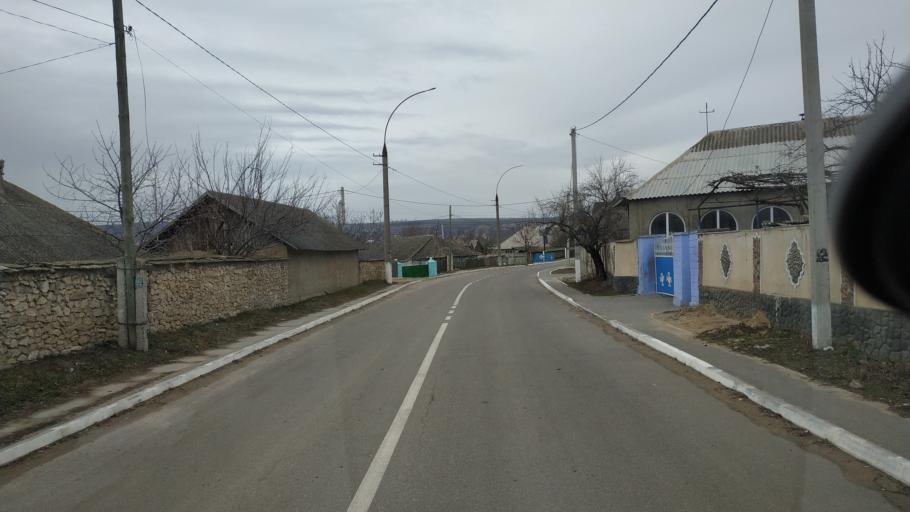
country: MD
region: Telenesti
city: Cocieri
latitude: 47.3466
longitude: 29.1117
